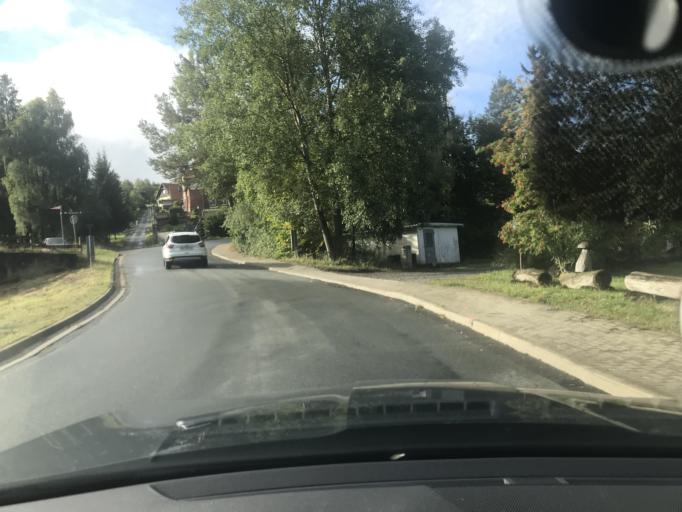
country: DE
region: Saxony-Anhalt
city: Harzgerode
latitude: 51.6282
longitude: 11.0915
